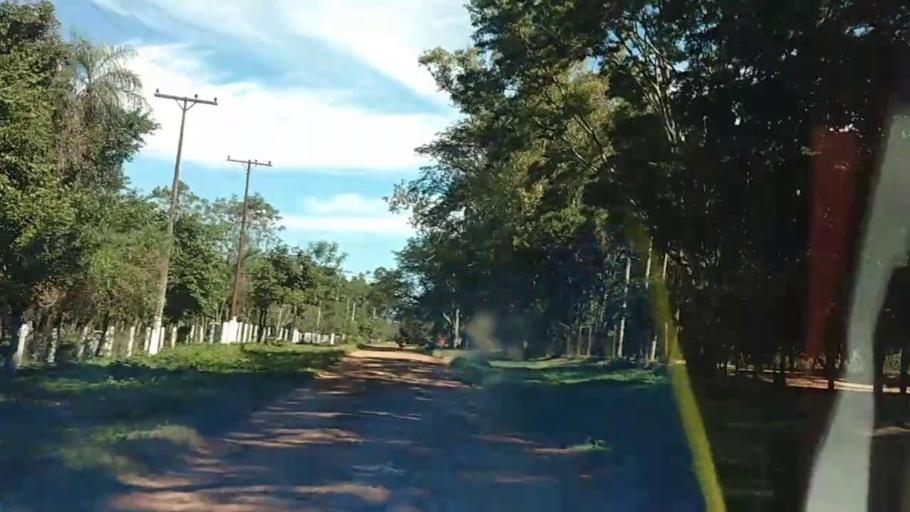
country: PY
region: Cordillera
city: San Bernardino
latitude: -25.3275
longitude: -57.2654
